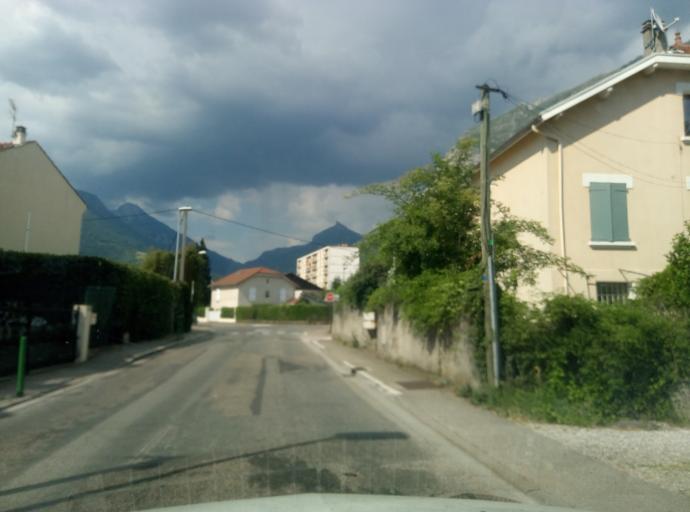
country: FR
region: Rhone-Alpes
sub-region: Departement de l'Isere
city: Saint-Egreve
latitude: 45.2221
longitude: 5.6822
